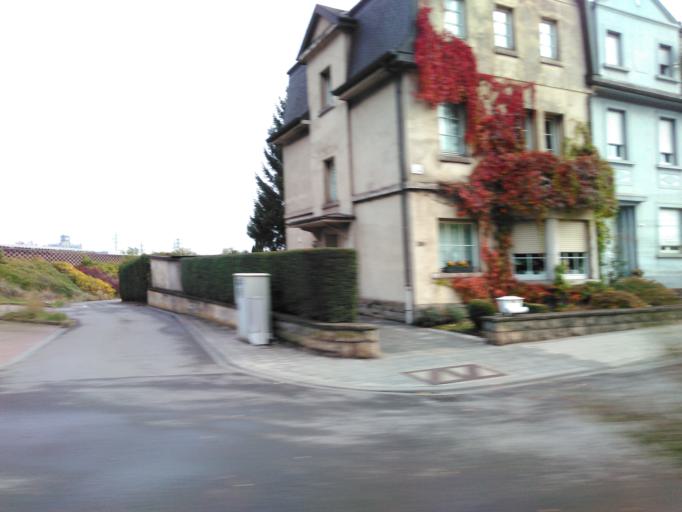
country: LU
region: Luxembourg
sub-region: Canton d'Esch-sur-Alzette
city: Esch-sur-Alzette
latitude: 49.5050
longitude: 5.9614
